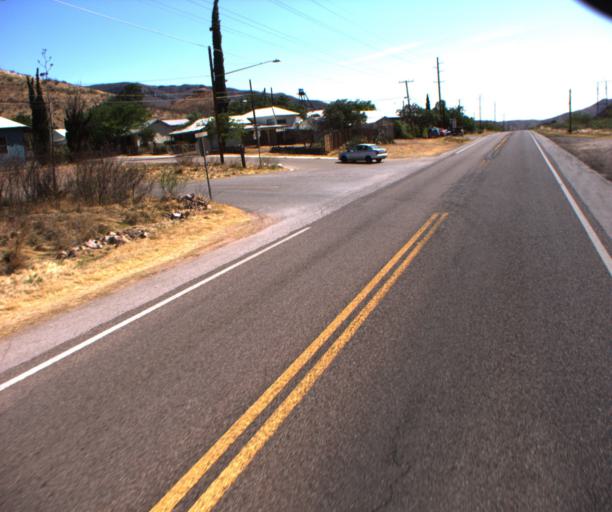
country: US
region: Arizona
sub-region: Cochise County
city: Bisbee
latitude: 31.4277
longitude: -109.8836
